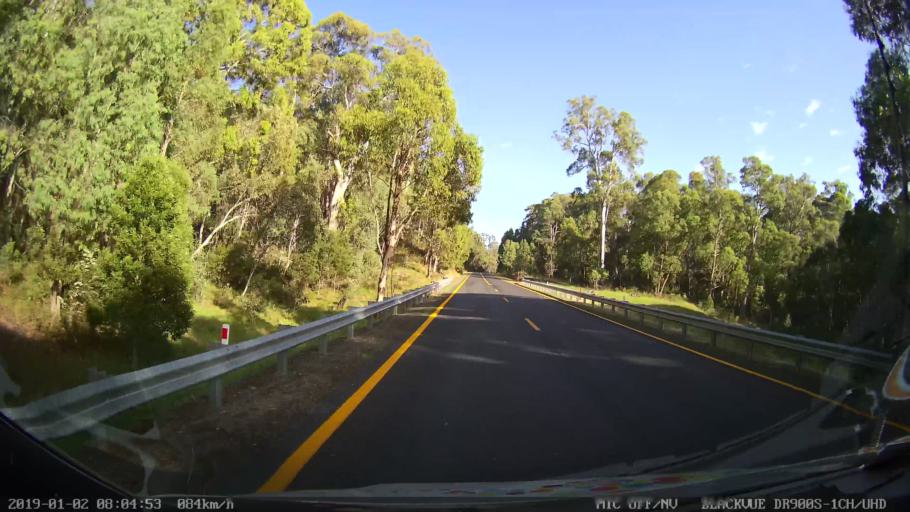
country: AU
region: New South Wales
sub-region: Tumut Shire
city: Tumut
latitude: -35.6576
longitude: 148.3909
